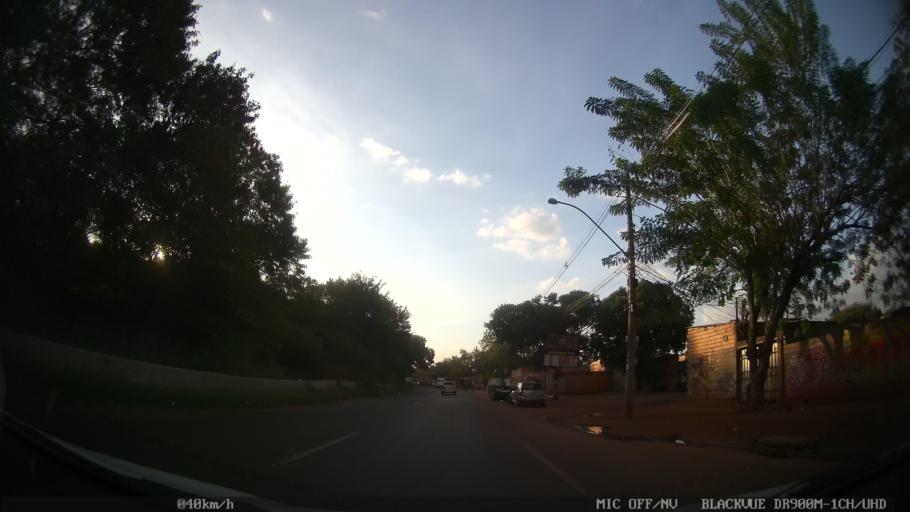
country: BR
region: Sao Paulo
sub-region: Ribeirao Preto
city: Ribeirao Preto
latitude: -21.1176
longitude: -47.8033
